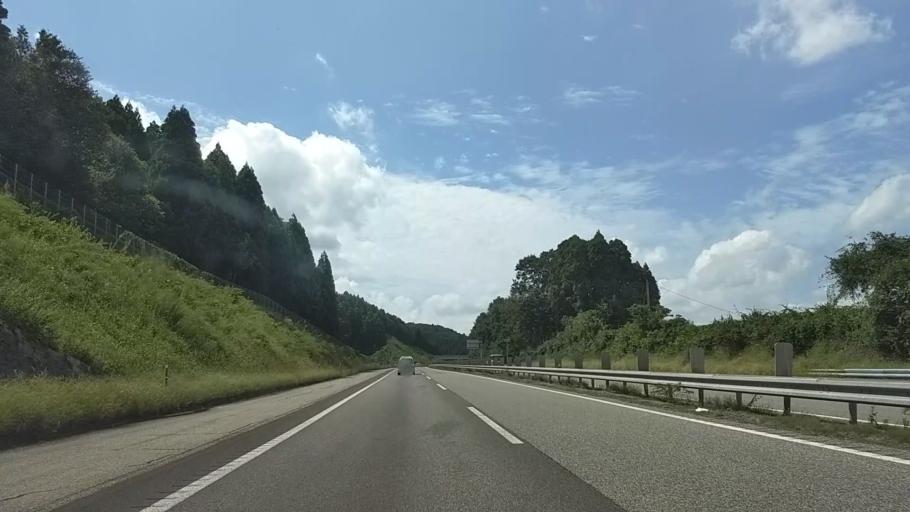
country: JP
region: Toyama
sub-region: Oyabe Shi
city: Oyabe
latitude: 36.6274
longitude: 136.8383
